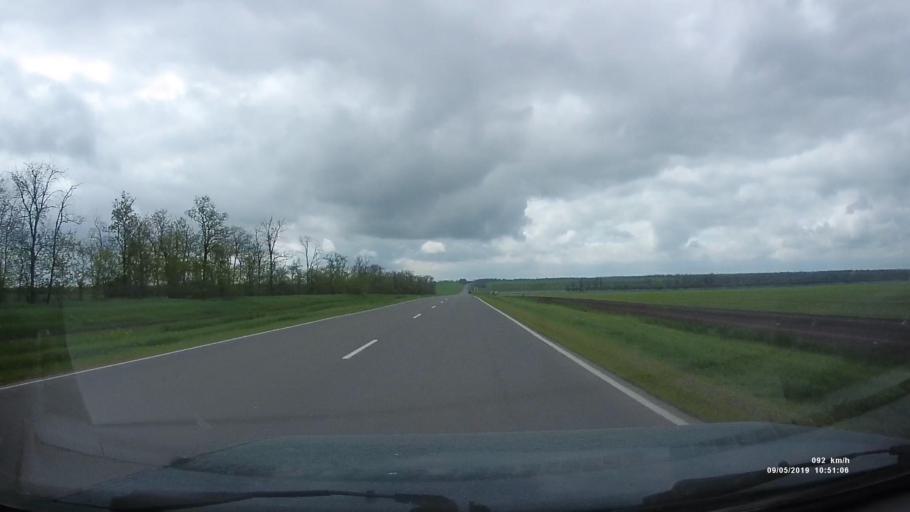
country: RU
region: Rostov
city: Peshkovo
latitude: 46.9193
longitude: 39.3553
